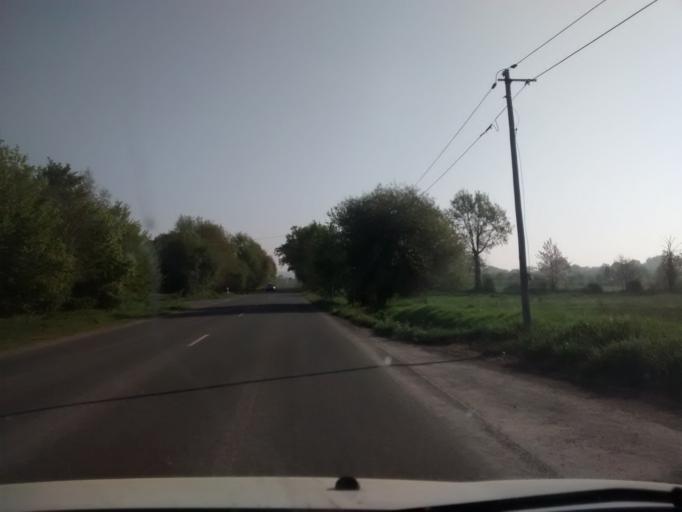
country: FR
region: Brittany
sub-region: Departement d'Ille-et-Vilaine
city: Saint-Jean-sur-Couesnon
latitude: 48.2810
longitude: -1.3821
